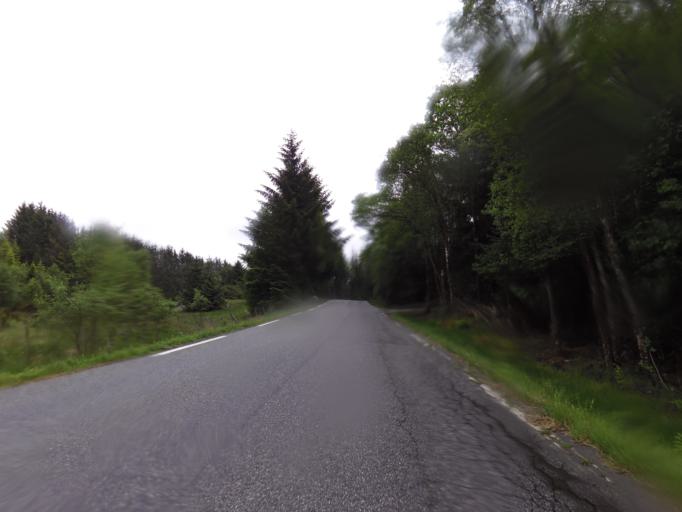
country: NO
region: Hordaland
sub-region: Sveio
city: Sveio
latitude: 59.5207
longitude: 5.2842
